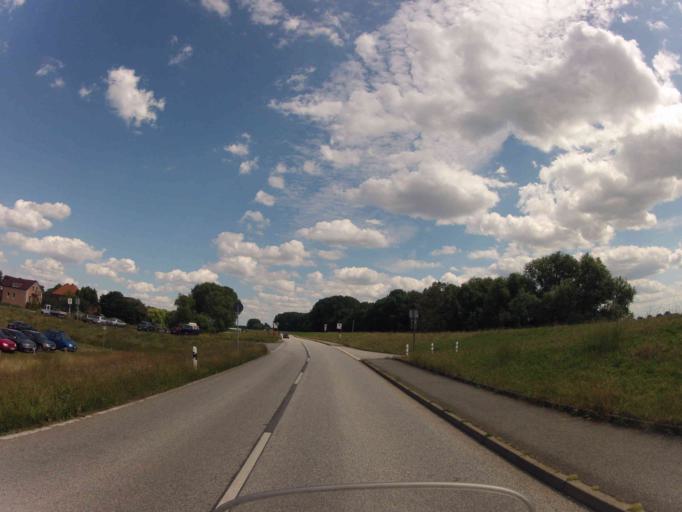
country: DE
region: Lower Saxony
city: Stelle
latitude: 53.4008
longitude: 10.1675
